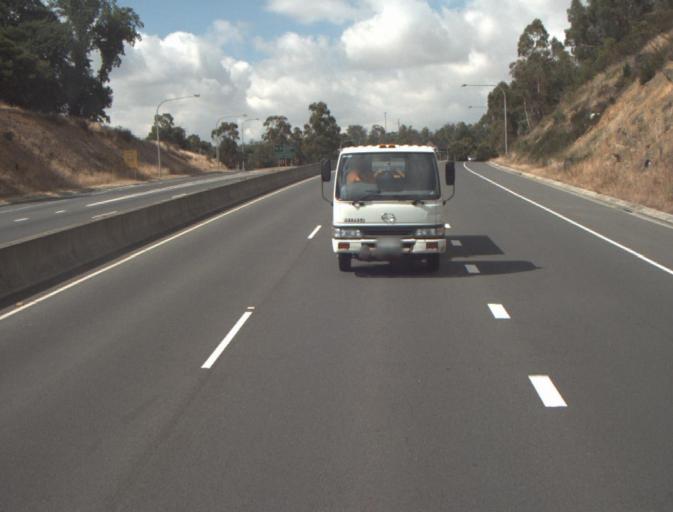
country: AU
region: Tasmania
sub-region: Launceston
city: Summerhill
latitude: -41.4684
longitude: 147.1428
